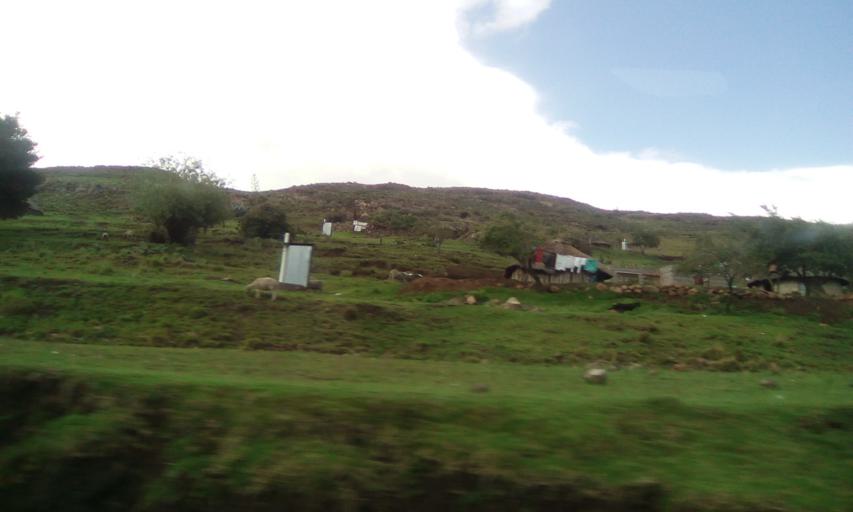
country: LS
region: Maseru
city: Nako
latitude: -29.6573
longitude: 27.8669
